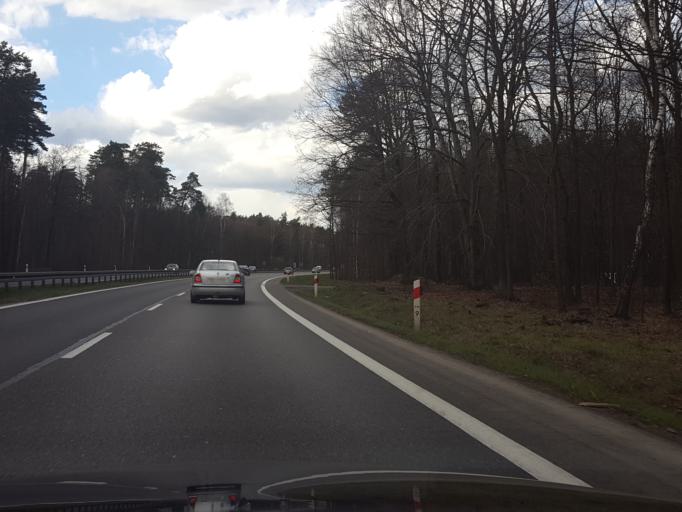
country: PL
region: Silesian Voivodeship
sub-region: Powiat pszczynski
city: Piasek
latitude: 50.0223
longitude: 18.9435
